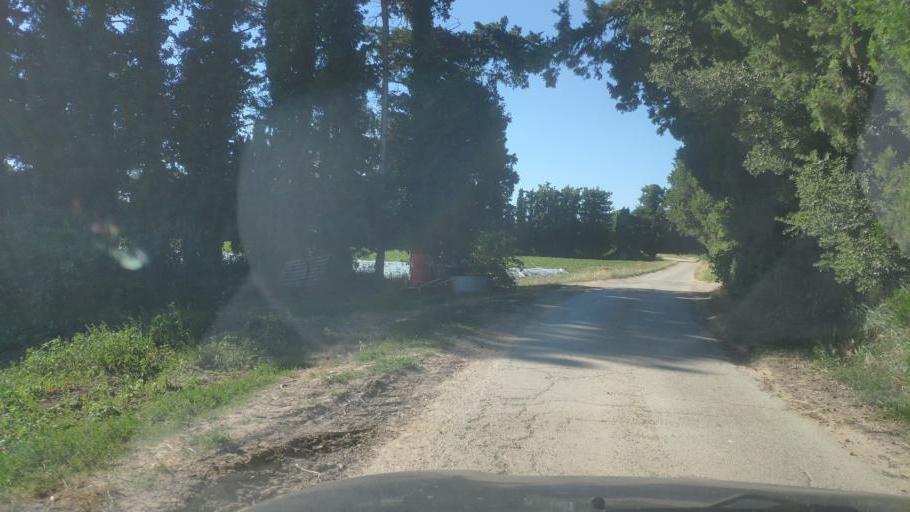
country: FR
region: Provence-Alpes-Cote d'Azur
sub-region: Departement du Vaucluse
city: Aubignan
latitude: 44.0813
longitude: 5.0203
